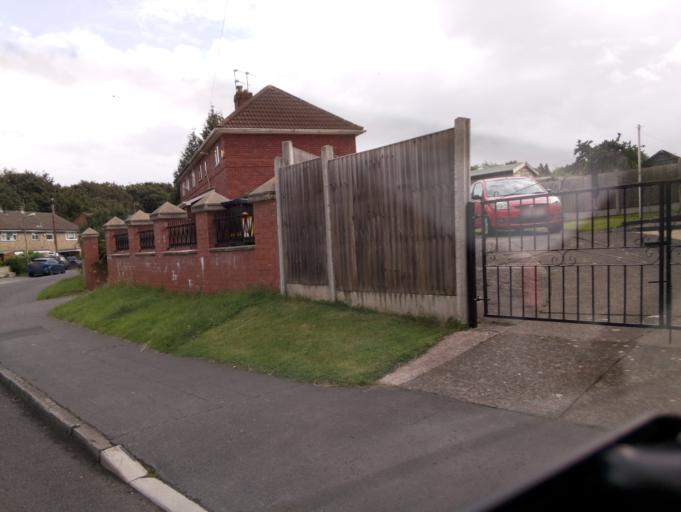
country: GB
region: England
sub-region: South Gloucestershire
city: Kingswood
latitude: 51.4495
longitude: -2.5387
